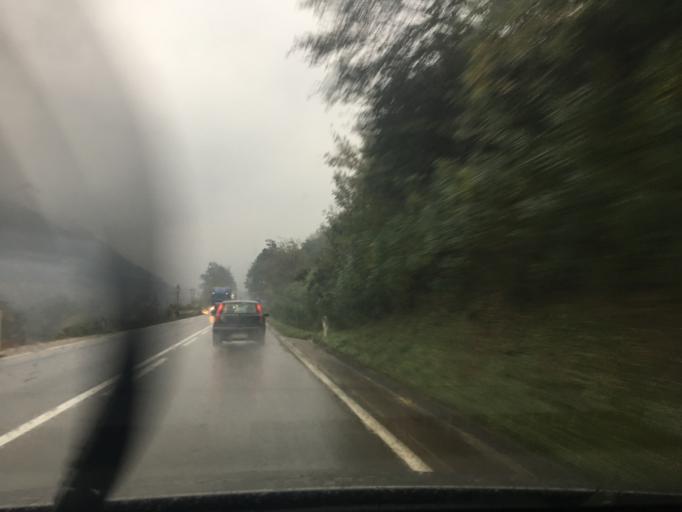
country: RS
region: Central Serbia
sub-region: Pcinjski Okrug
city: Vladicin Han
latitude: 42.8177
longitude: 22.1220
